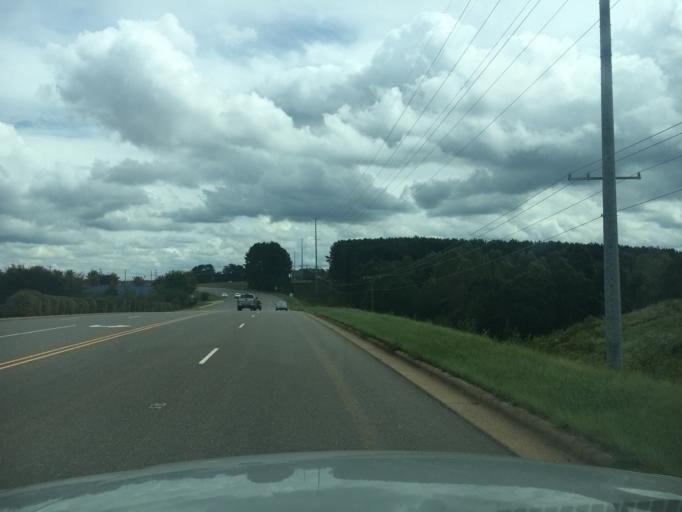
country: US
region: North Carolina
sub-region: Catawba County
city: Hickory
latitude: 35.6979
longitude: -81.2958
